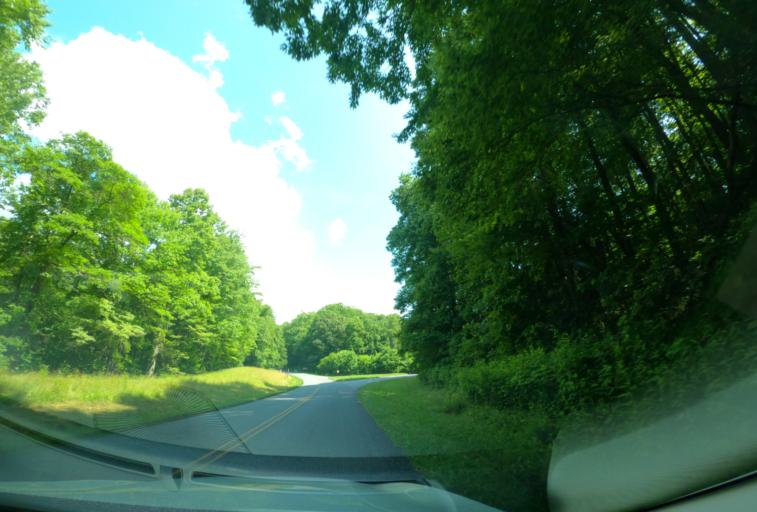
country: US
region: North Carolina
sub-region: Haywood County
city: Maggie Valley
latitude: 35.4399
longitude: -83.0800
